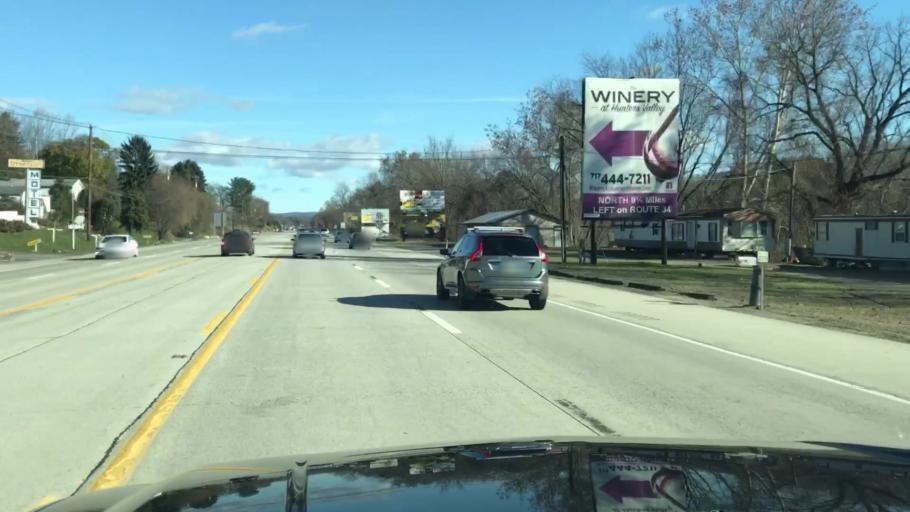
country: US
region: Pennsylvania
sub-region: Perry County
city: Duncannon
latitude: 40.4335
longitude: -76.9993
